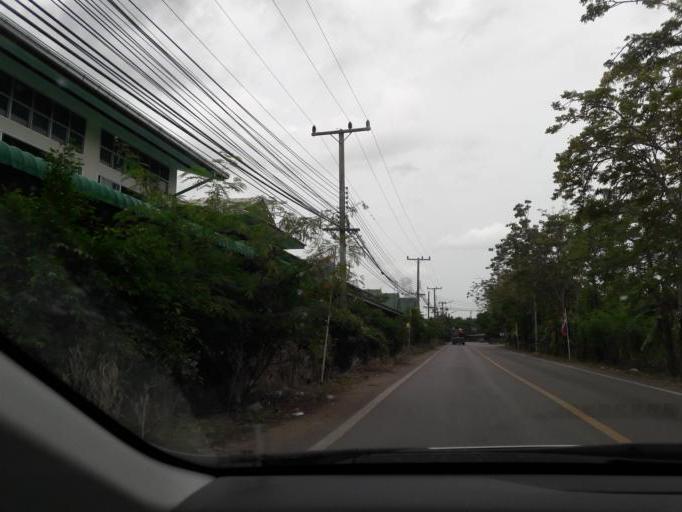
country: TH
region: Samut Sakhon
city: Ban Phaeo
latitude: 13.5829
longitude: 100.0299
